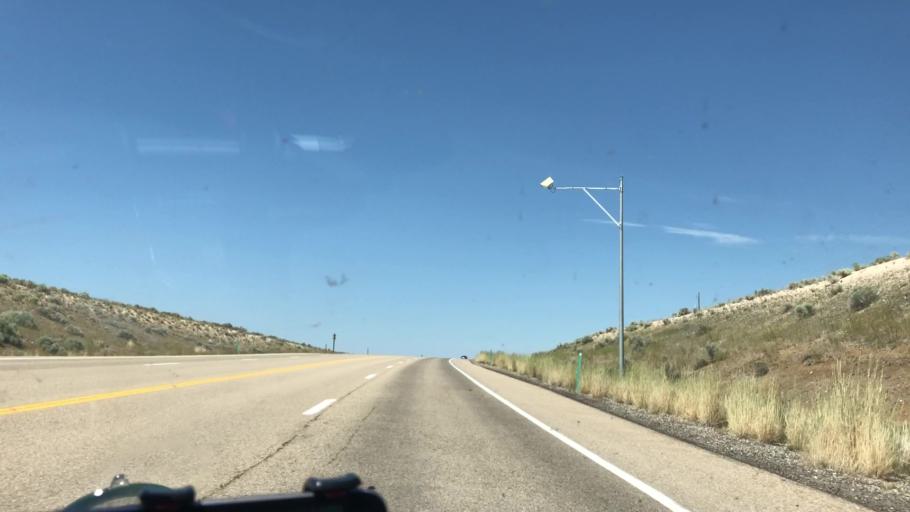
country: US
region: Idaho
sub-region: Owyhee County
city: Marsing
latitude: 43.2945
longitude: -116.9856
